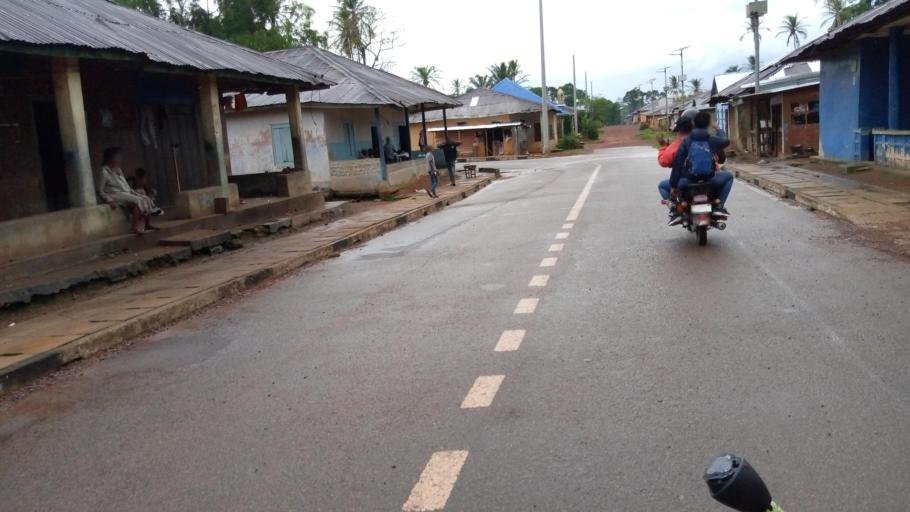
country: SL
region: Southern Province
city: Moyamba
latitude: 8.1623
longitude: -12.4345
